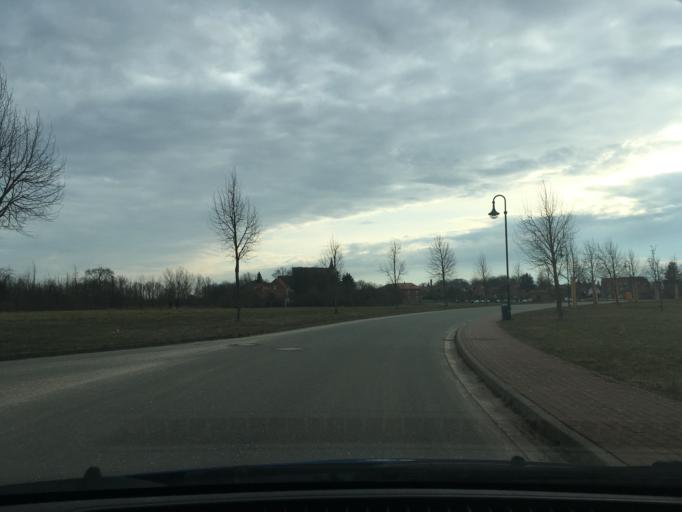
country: DE
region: Mecklenburg-Vorpommern
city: Zarrentin
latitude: 53.5582
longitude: 10.9179
